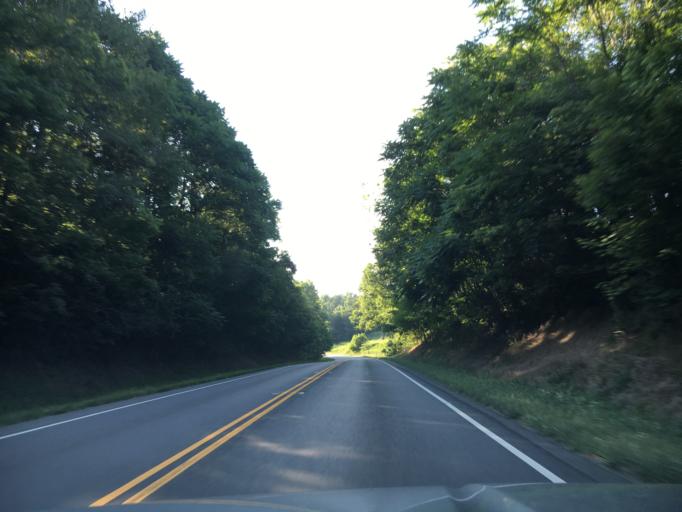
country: US
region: Virginia
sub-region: City of Bedford
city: Bedford
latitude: 37.2339
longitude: -79.5749
